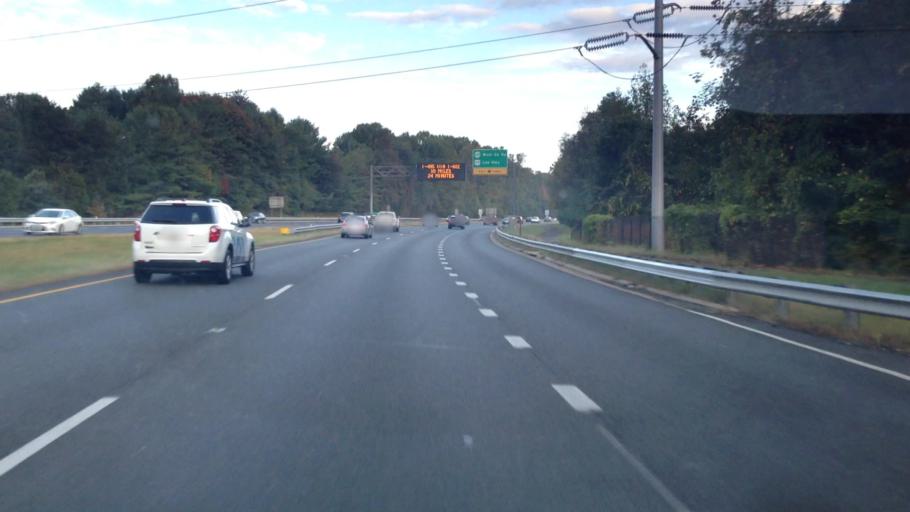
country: US
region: Virginia
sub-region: Fairfax County
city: Greenbriar
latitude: 38.8330
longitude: -77.3707
